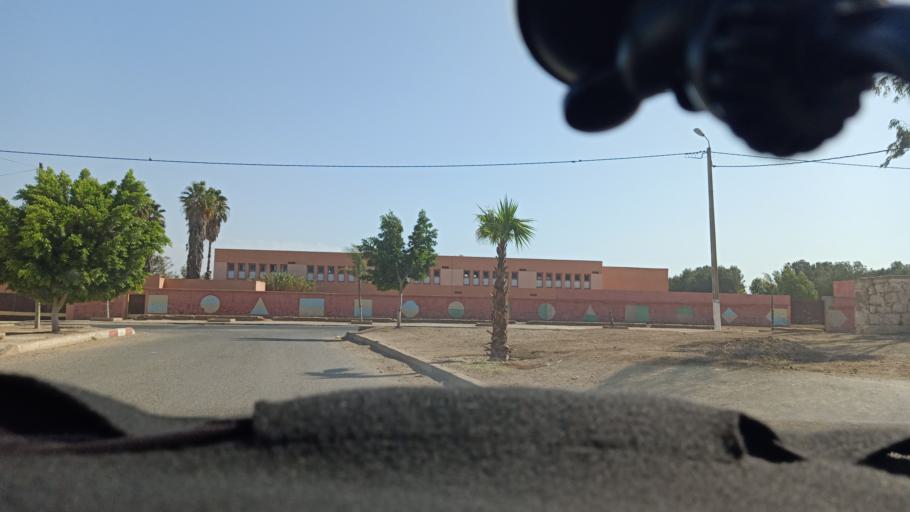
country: MA
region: Doukkala-Abda
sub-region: Safi
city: Youssoufia
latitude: 32.3478
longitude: -8.8345
